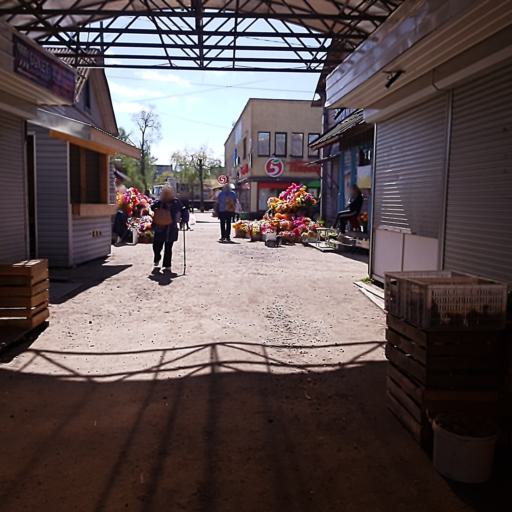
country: RU
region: Republic of Karelia
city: Lakhdenpokh'ya
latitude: 61.5206
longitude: 30.1962
